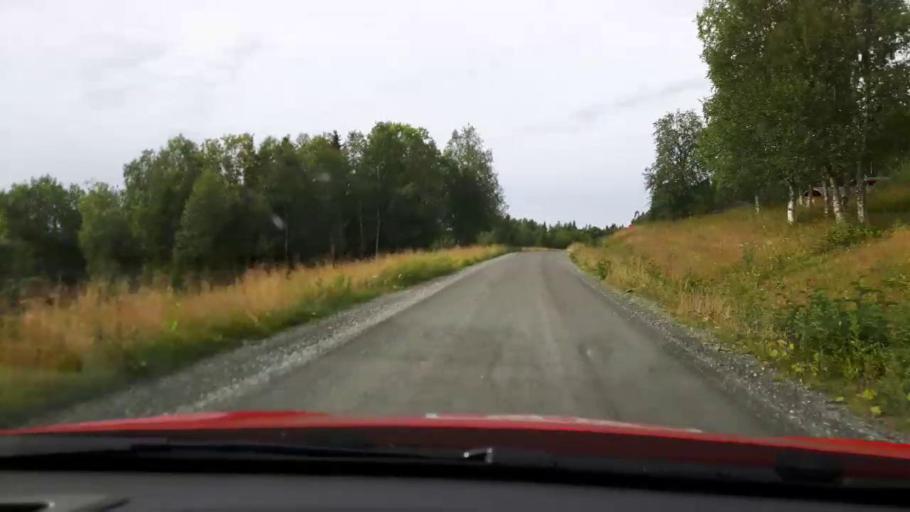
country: SE
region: Jaemtland
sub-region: Are Kommun
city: Are
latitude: 63.7448
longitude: 12.9793
